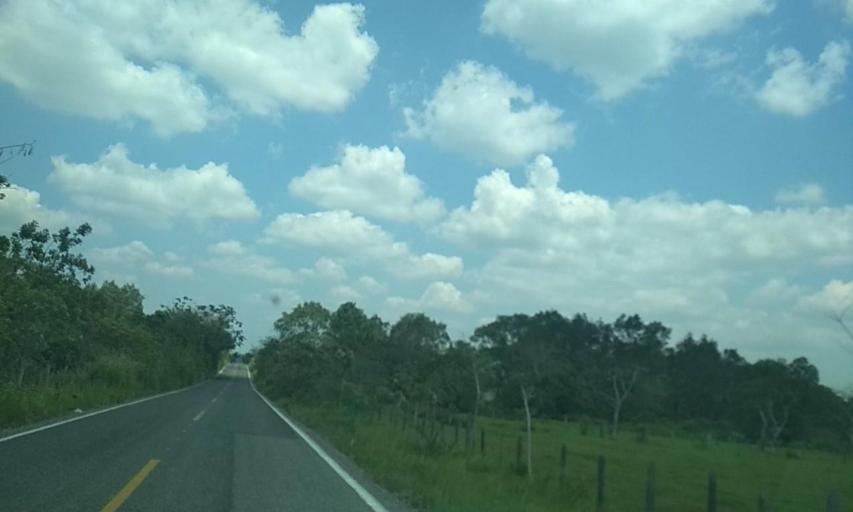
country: MX
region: Tabasco
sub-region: Huimanguillo
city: Huapacal 1ra. Seccion
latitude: 17.7536
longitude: -93.7438
